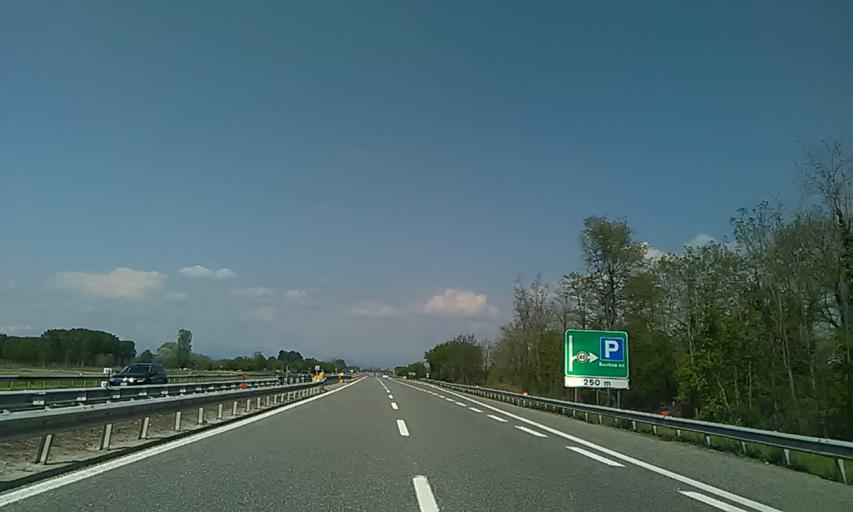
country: IT
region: Piedmont
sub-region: Provincia di Novara
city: Landiona
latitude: 45.4993
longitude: 8.4382
